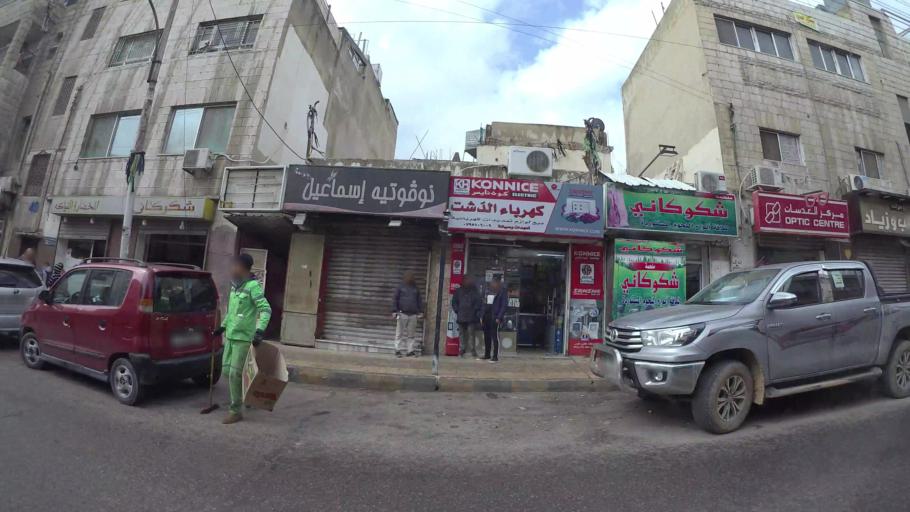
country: JO
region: Amman
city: Amman
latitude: 31.9757
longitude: 35.9253
